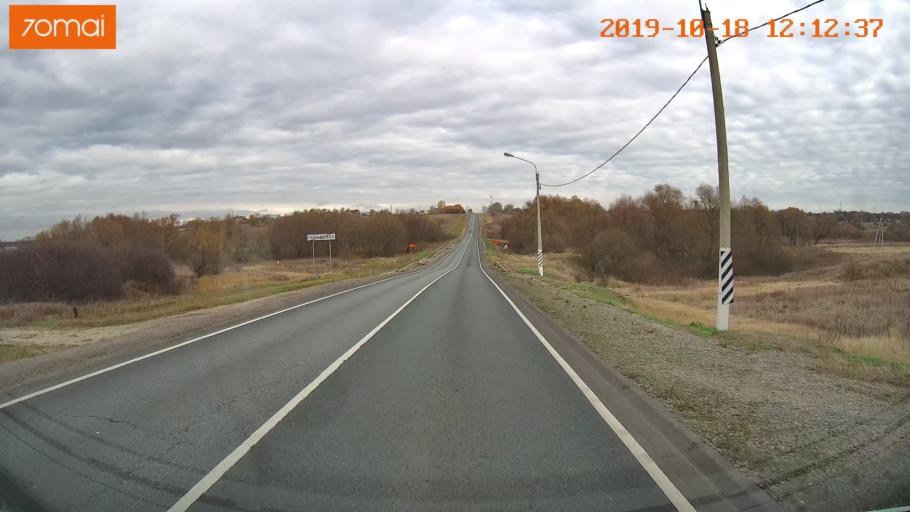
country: RU
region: Rjazan
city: Zakharovo
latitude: 54.4134
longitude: 39.3602
